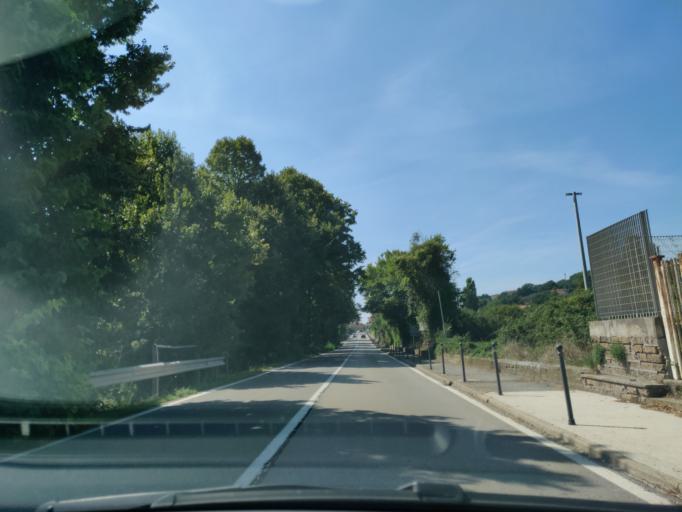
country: IT
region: Latium
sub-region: Provincia di Viterbo
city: Monte Romano
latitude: 42.2732
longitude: 11.9074
